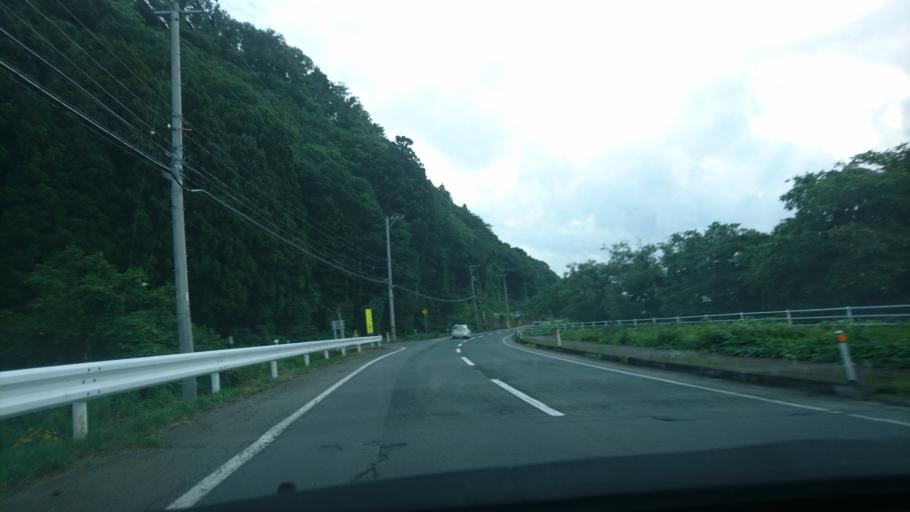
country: JP
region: Iwate
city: Kitakami
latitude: 39.2955
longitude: 141.1485
